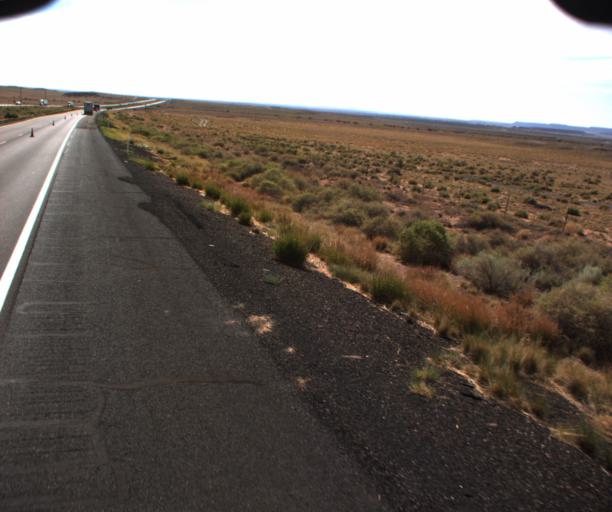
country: US
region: Arizona
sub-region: Navajo County
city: Holbrook
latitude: 34.9907
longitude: -109.9959
